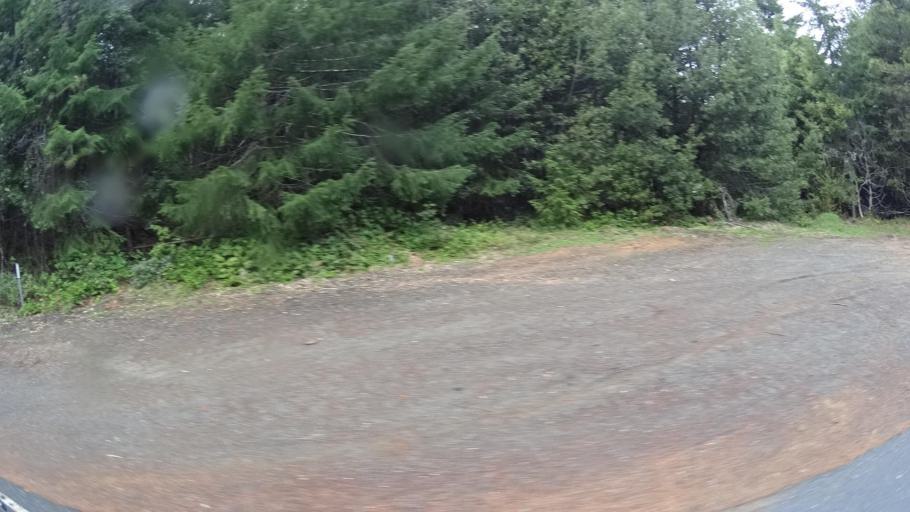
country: US
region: California
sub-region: Humboldt County
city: Willow Creek
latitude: 41.1983
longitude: -123.8069
